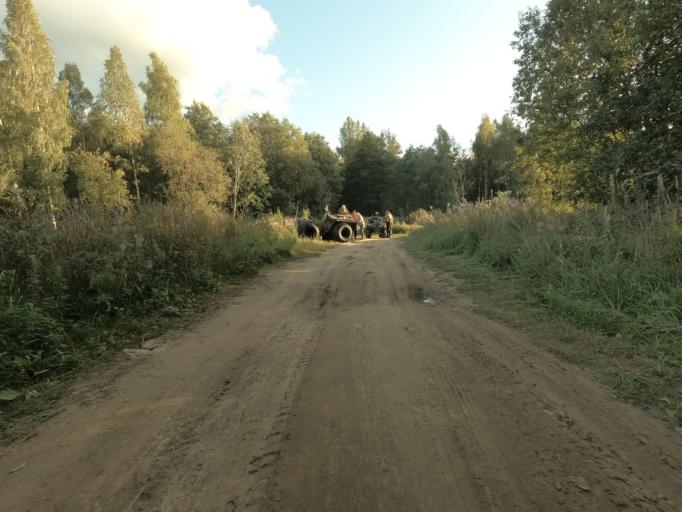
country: RU
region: Leningrad
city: Otradnoye
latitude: 59.8543
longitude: 30.7953
